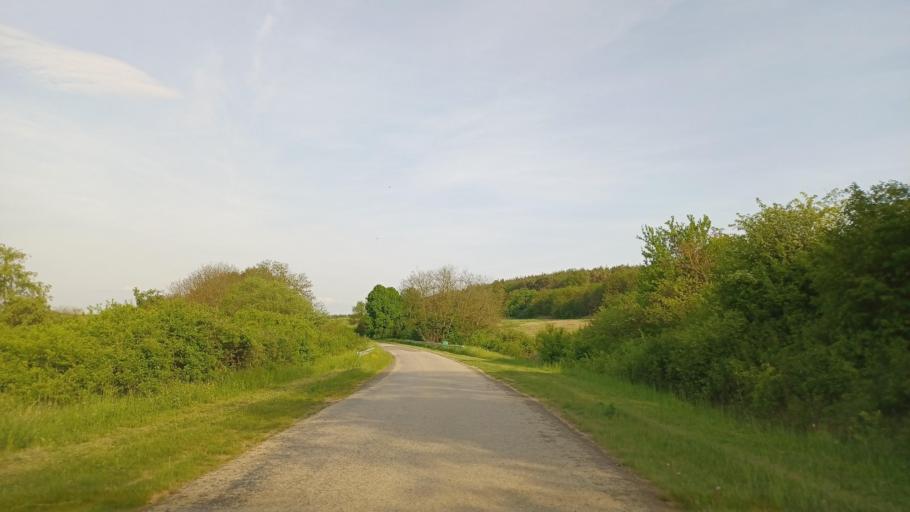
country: HU
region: Baranya
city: Kozarmisleny
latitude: 45.9642
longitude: 18.3687
